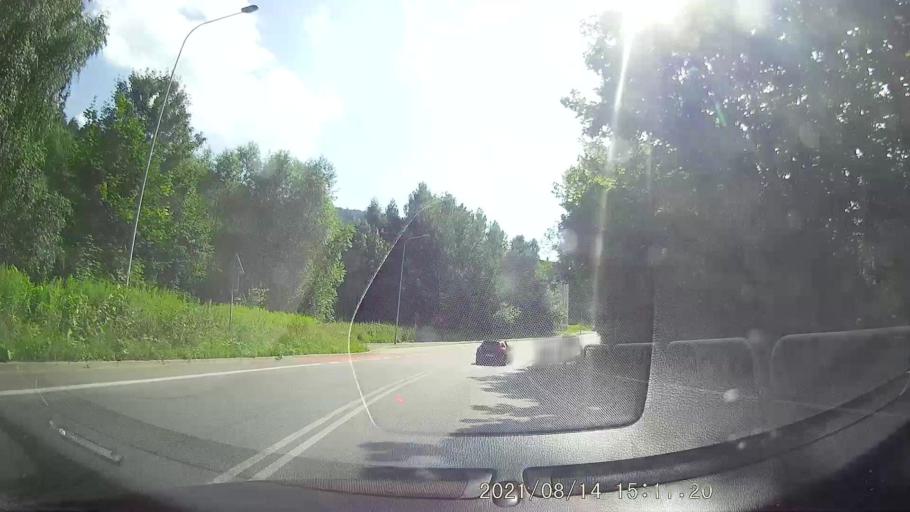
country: PL
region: Lower Silesian Voivodeship
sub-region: Powiat walbrzyski
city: Walbrzych
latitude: 50.7565
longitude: 16.3176
